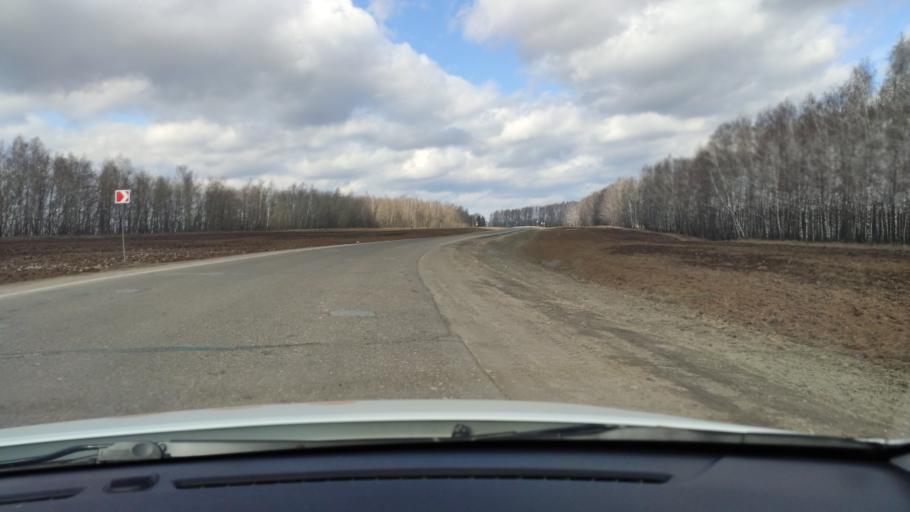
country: RU
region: Tatarstan
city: Vysokaya Gora
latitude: 56.0960
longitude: 49.1832
